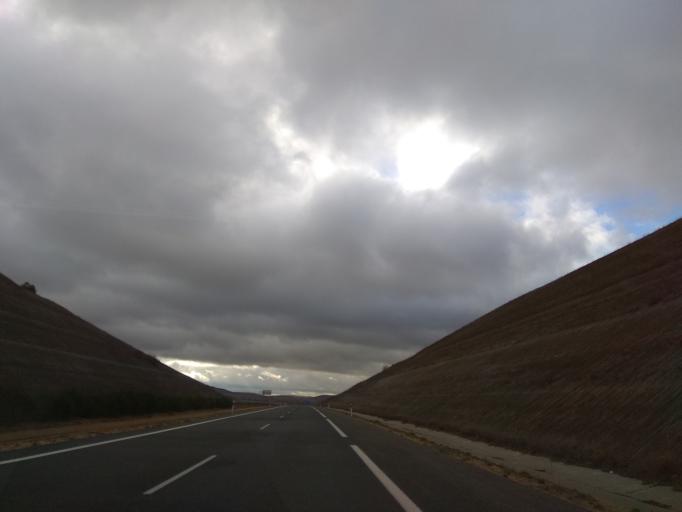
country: ES
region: Castille and Leon
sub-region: Provincia de Burgos
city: Quintanaortuno
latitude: 42.4504
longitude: -3.6907
